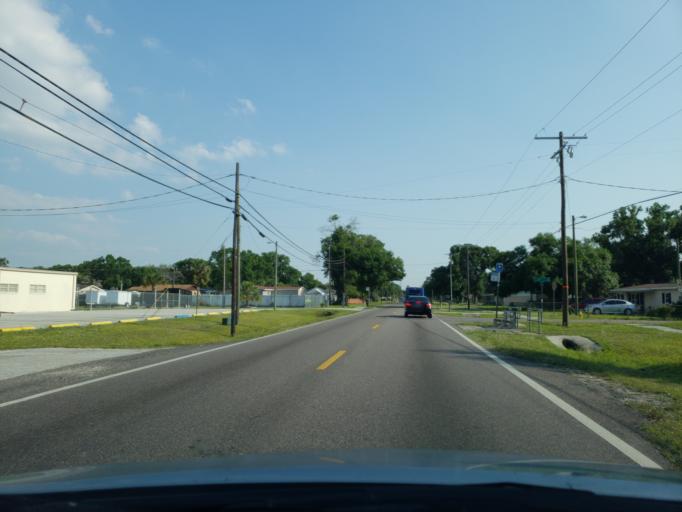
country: US
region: Florida
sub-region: Hillsborough County
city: Palm River-Clair Mel
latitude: 27.9180
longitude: -82.3687
